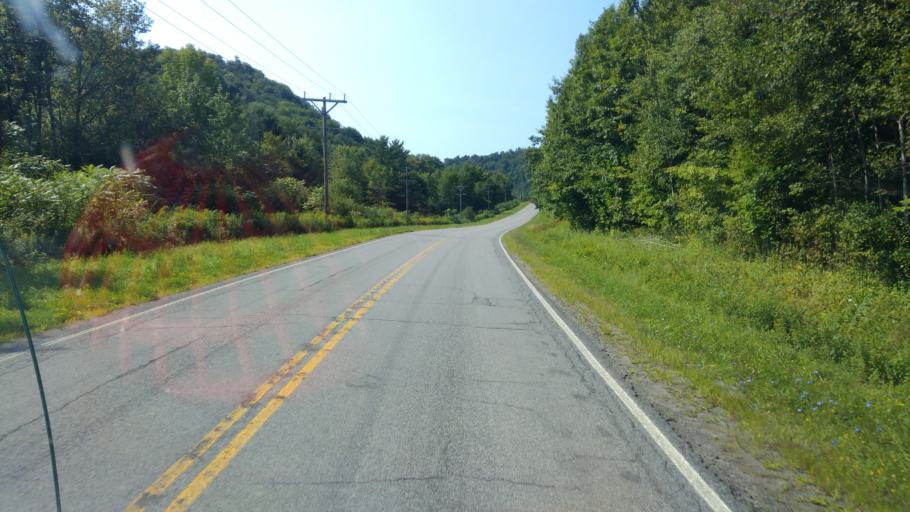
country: US
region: New York
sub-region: Allegany County
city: Bolivar
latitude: 42.1239
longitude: -78.1565
